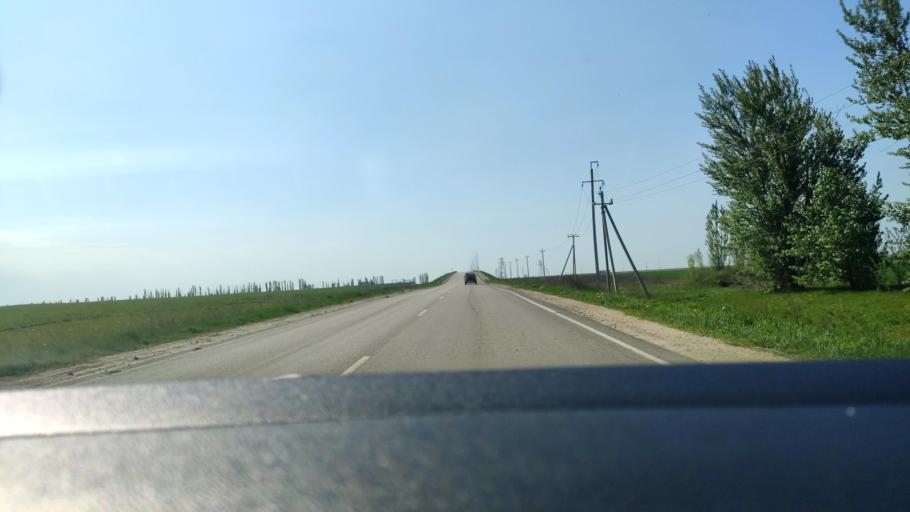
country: RU
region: Voronezj
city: Novaya Usman'
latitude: 51.5964
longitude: 39.3739
